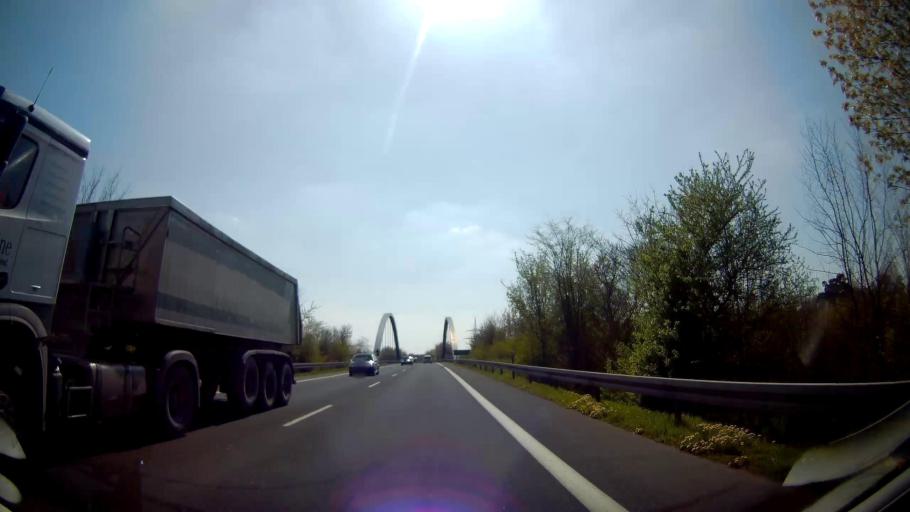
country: DE
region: North Rhine-Westphalia
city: Marl
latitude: 51.6690
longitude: 7.0284
